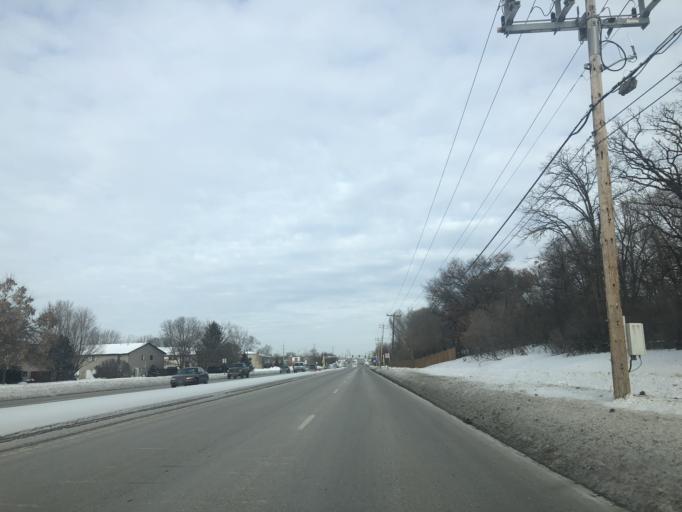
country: US
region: Minnesota
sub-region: Anoka County
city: Lexington
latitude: 45.1502
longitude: -93.1634
